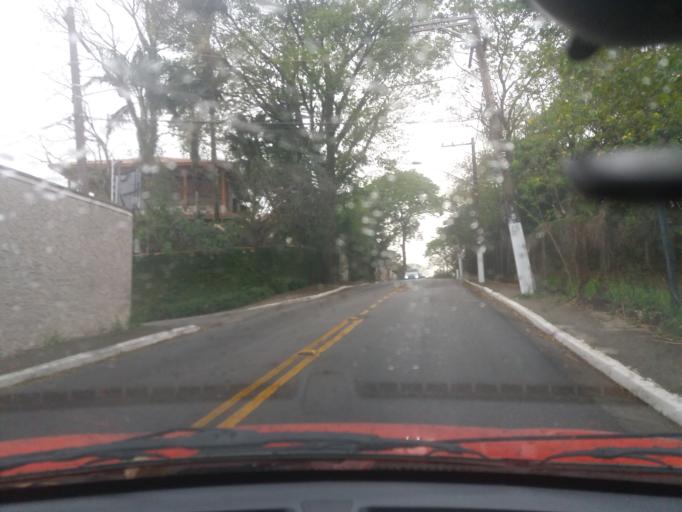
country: BR
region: Sao Paulo
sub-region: Sao Paulo
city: Sao Paulo
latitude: -23.4628
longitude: -46.6246
